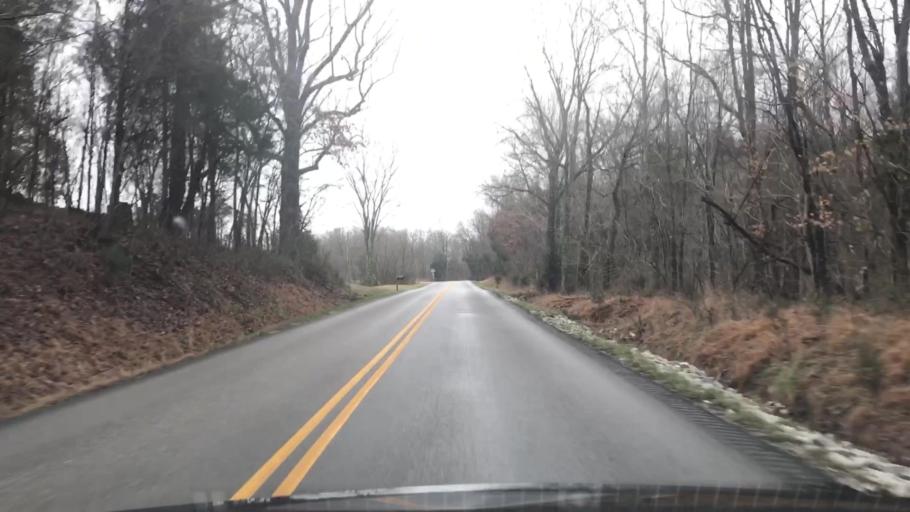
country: US
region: Kentucky
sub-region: Barren County
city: Glasgow
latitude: 36.8866
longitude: -85.7910
